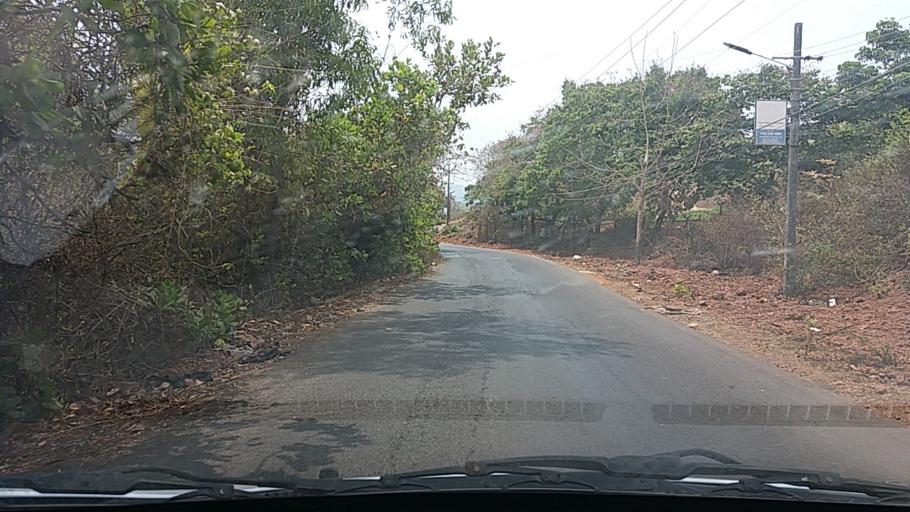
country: IN
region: Goa
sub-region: North Goa
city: Saligao
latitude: 15.5325
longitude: 73.7995
